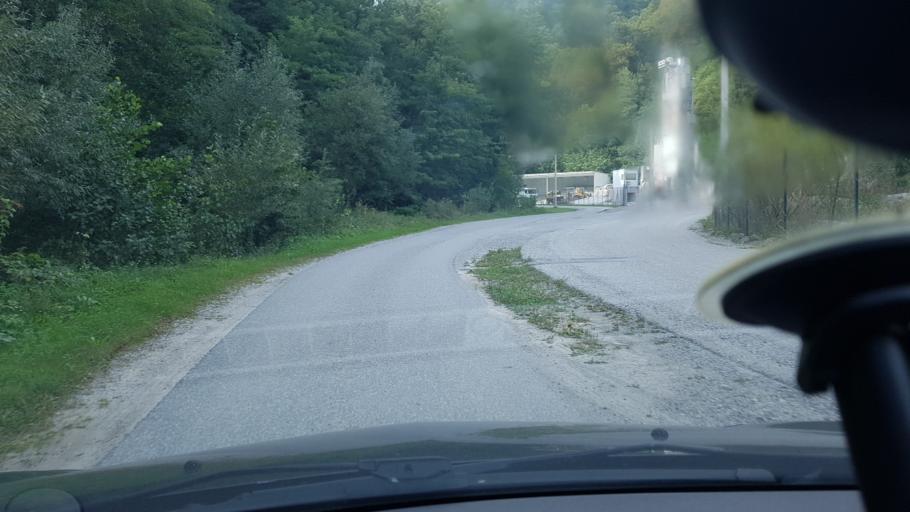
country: HR
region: Krapinsko-Zagorska
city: Mihovljan
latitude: 46.1851
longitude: 15.9811
